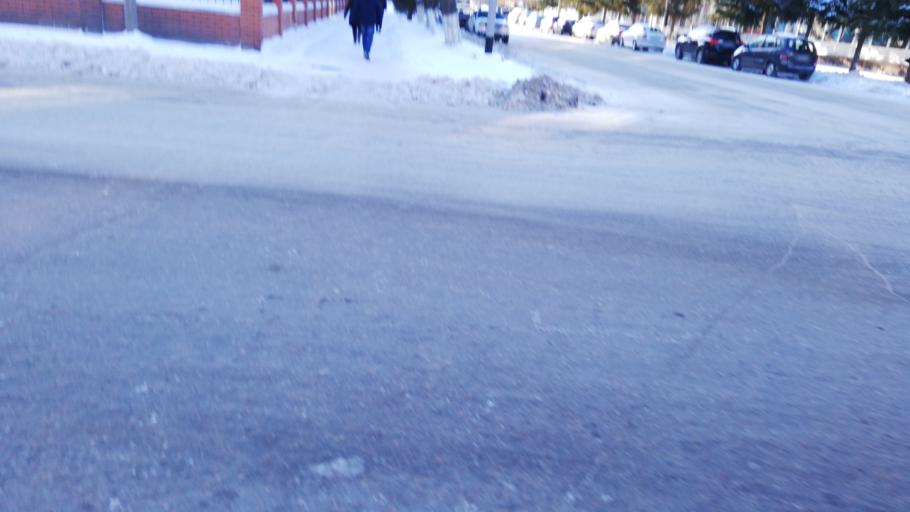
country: KZ
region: Soltustik Qazaqstan
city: Petropavlovsk
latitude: 54.8647
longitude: 69.1406
